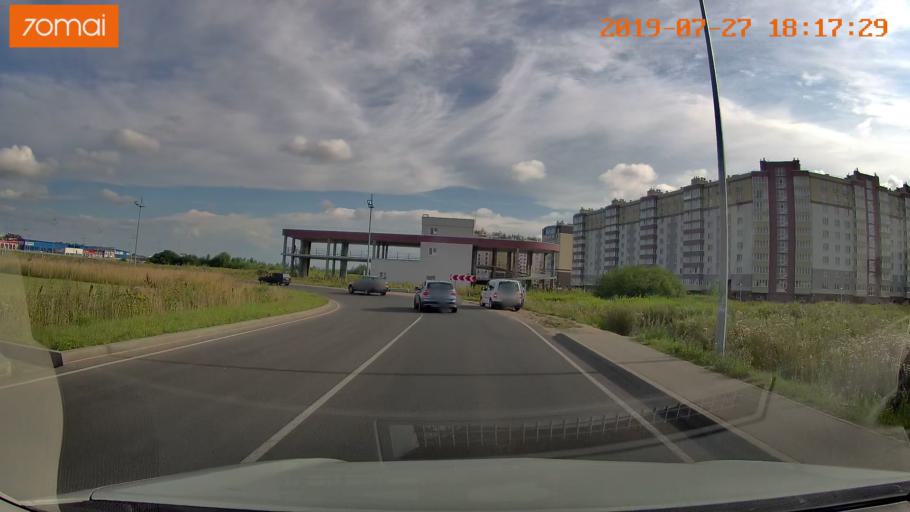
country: RU
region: Kaliningrad
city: Bol'shoe Isakovo
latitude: 54.7150
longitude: 20.5946
